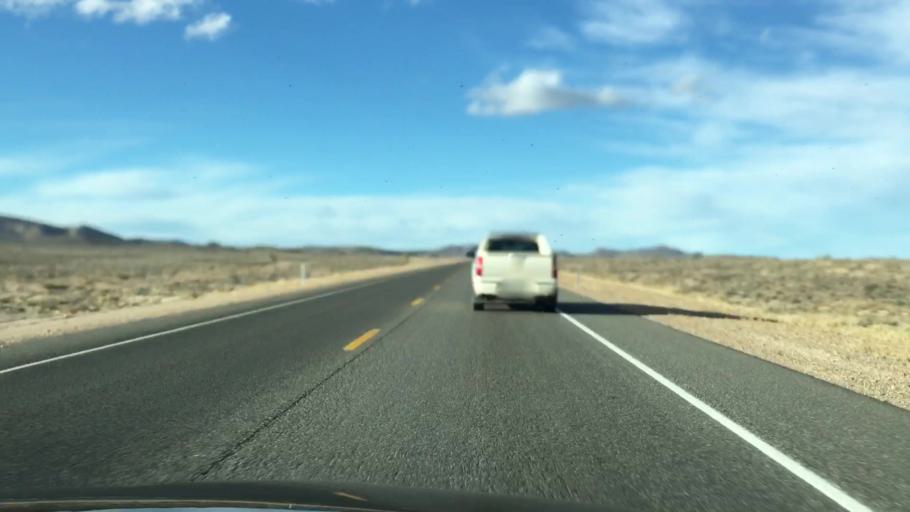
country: US
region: Nevada
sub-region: Esmeralda County
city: Goldfield
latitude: 37.5813
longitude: -117.2053
